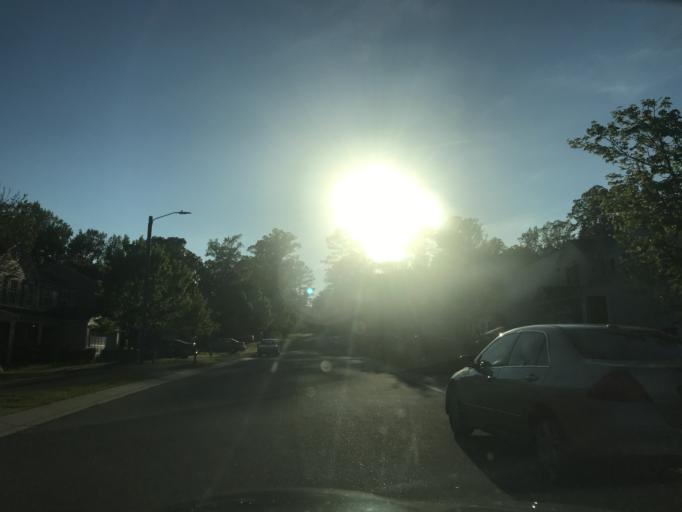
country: US
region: North Carolina
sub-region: Wake County
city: Raleigh
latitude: 35.8272
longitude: -78.5643
